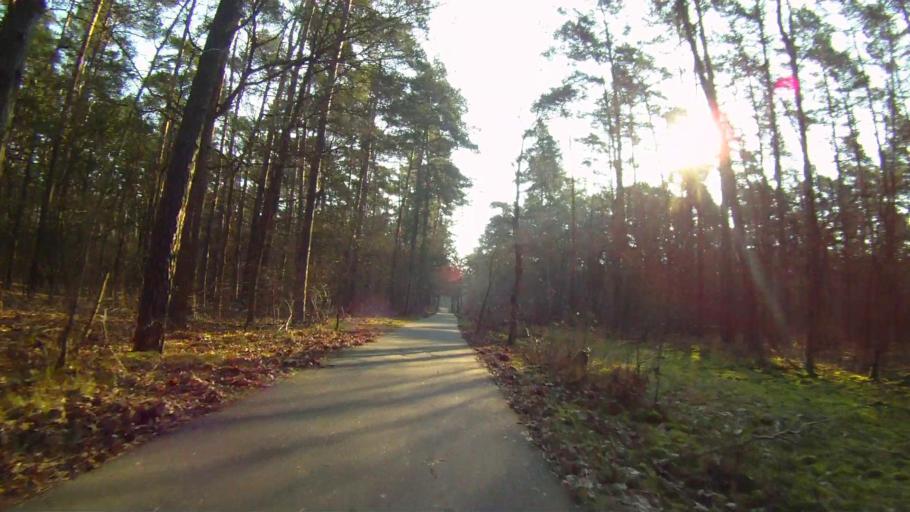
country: DE
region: Berlin
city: Rahnsdorf
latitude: 52.4252
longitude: 13.6843
